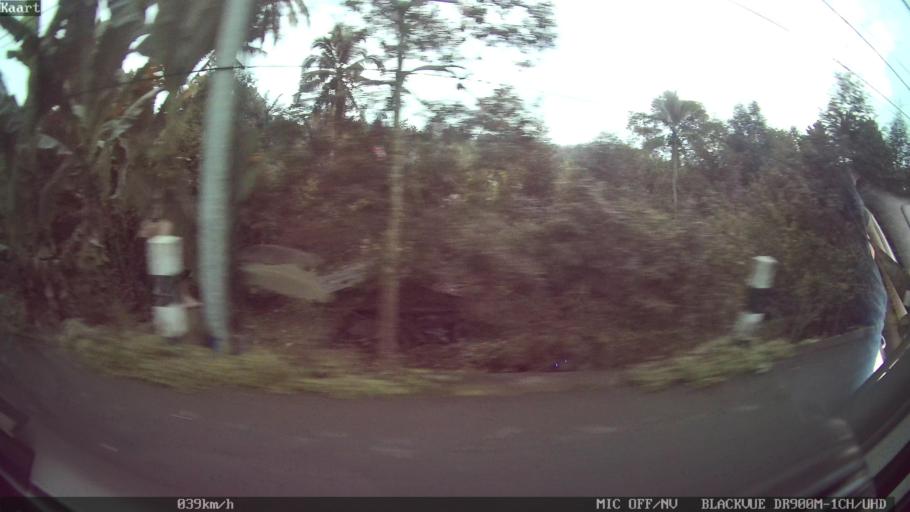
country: ID
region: Bali
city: Peneng
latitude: -8.3484
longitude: 115.1845
